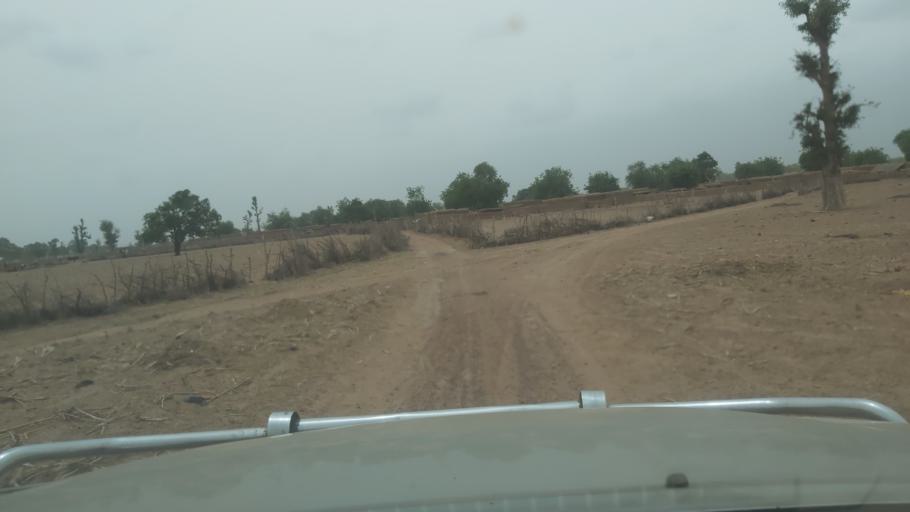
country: ML
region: Koulikoro
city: Banamba
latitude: 13.3761
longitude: -7.2250
